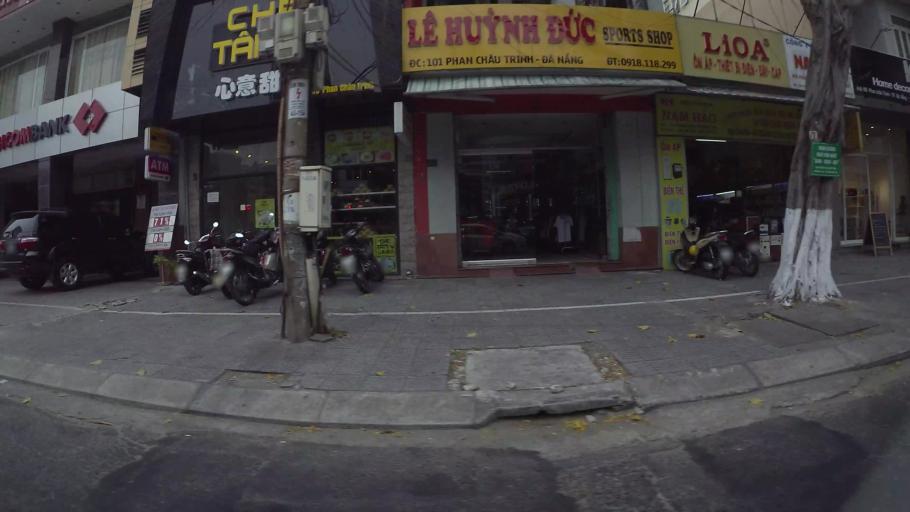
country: VN
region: Da Nang
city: Da Nang
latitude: 16.0660
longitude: 108.2202
